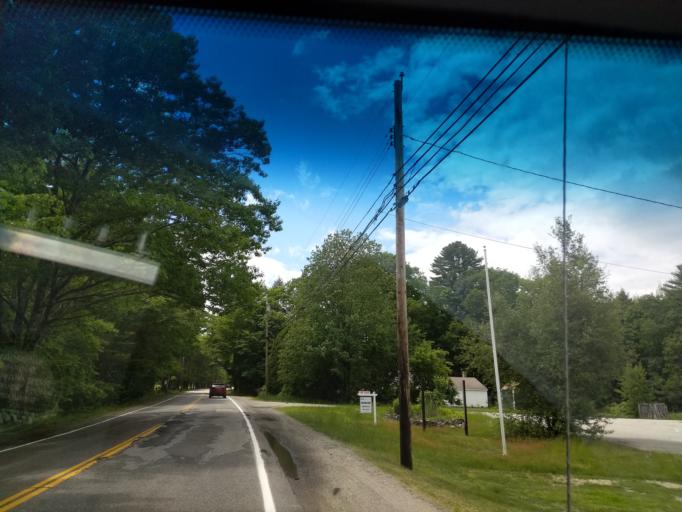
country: US
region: Maine
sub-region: Cumberland County
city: South Portland Gardens
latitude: 43.6227
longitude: -70.3601
